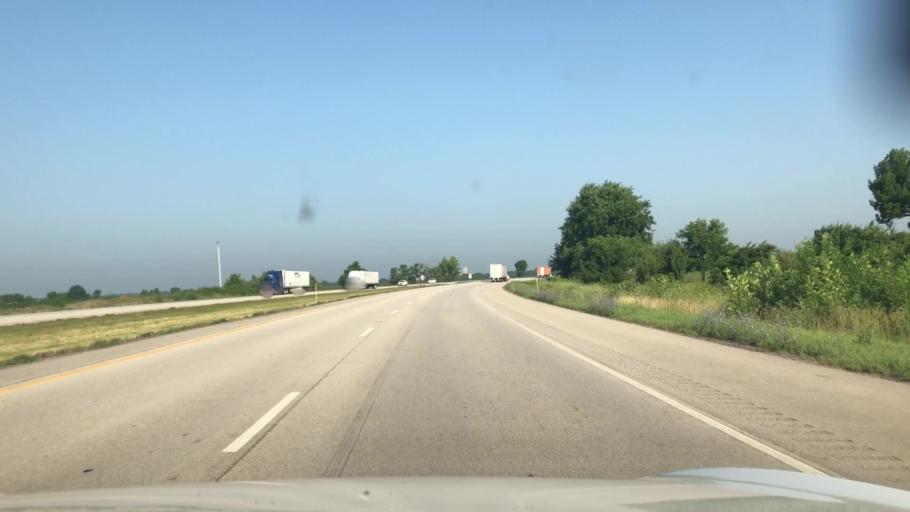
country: US
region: Illinois
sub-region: De Witt County
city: Farmer City
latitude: 40.2381
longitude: -88.6059
